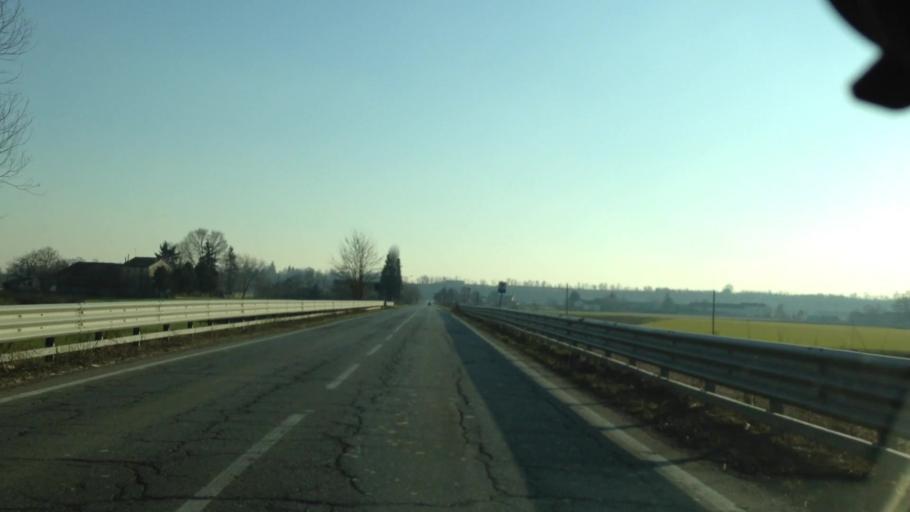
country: IT
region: Piedmont
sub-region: Provincia di Alessandria
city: Felizzano
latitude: 44.8843
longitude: 8.4419
